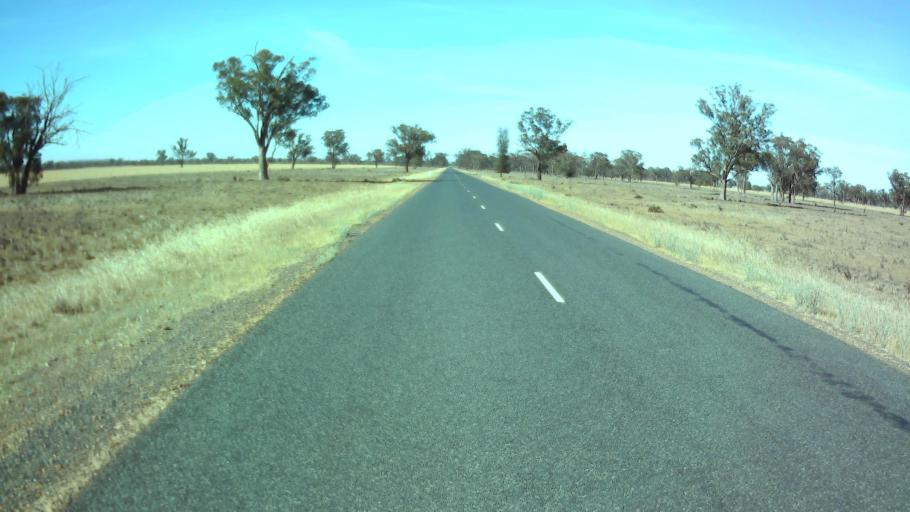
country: AU
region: New South Wales
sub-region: Weddin
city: Grenfell
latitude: -34.0824
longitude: 147.8950
